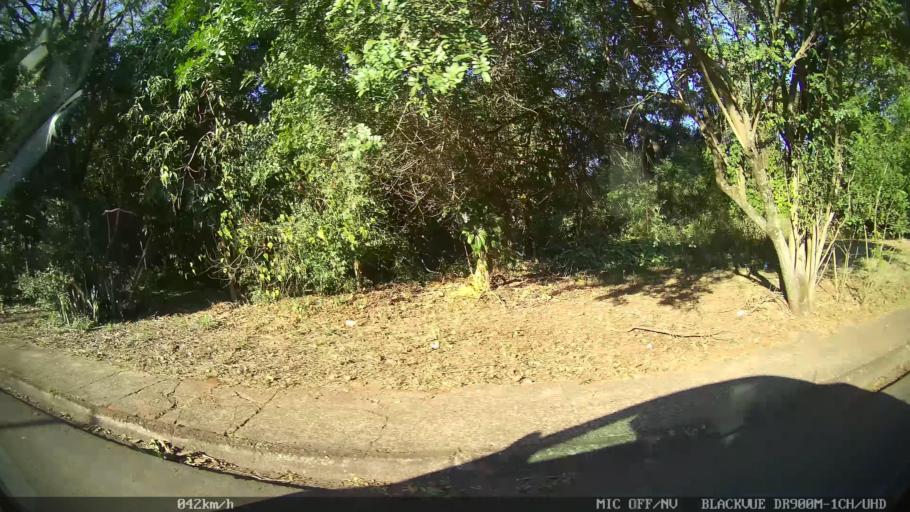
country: BR
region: Sao Paulo
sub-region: Piracicaba
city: Piracicaba
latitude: -22.6863
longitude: -47.6333
